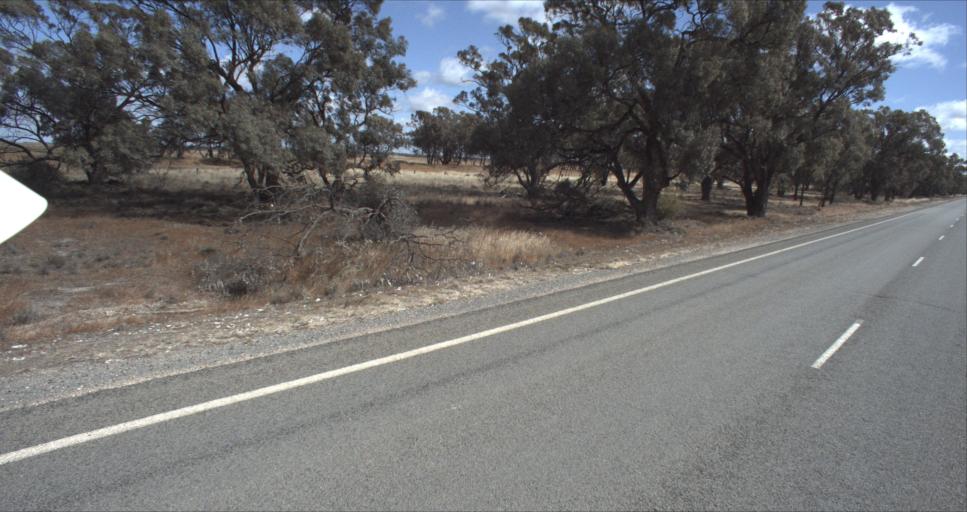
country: AU
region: New South Wales
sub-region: Murrumbidgee Shire
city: Darlington Point
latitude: -34.5672
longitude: 146.1679
